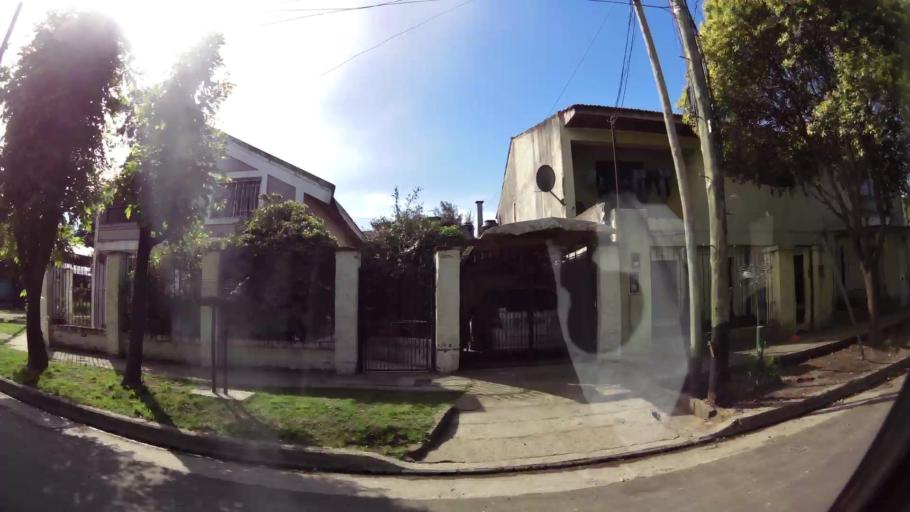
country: AR
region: Buenos Aires
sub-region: Partido de Almirante Brown
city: Adrogue
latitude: -34.7993
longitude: -58.3508
